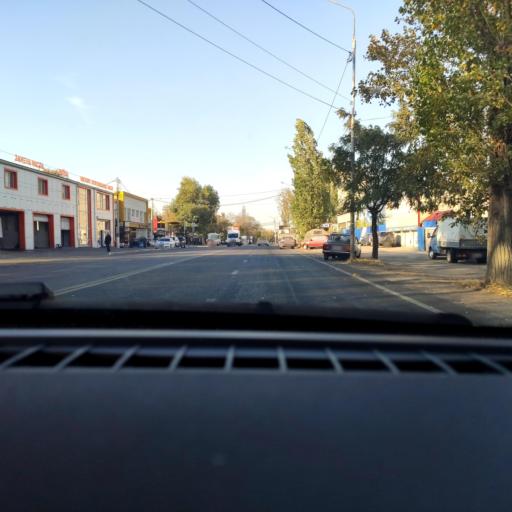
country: RU
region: Voronezj
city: Maslovka
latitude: 51.5976
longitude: 39.2522
